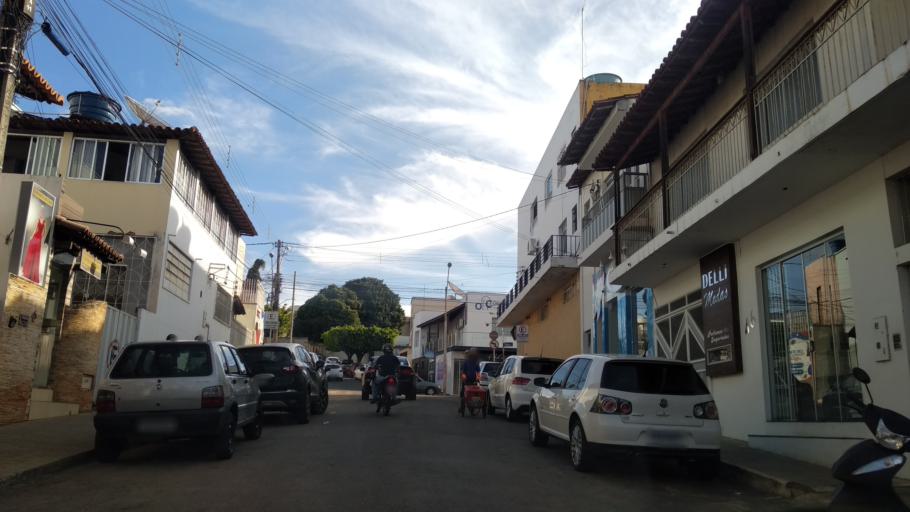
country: BR
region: Bahia
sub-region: Caetite
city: Caetite
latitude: -14.0685
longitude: -42.4899
